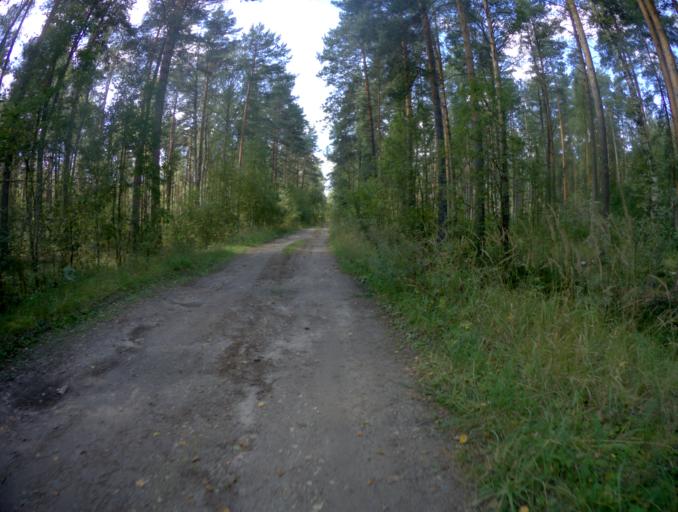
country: RU
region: Vladimir
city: Nikologory
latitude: 56.0182
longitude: 41.9133
